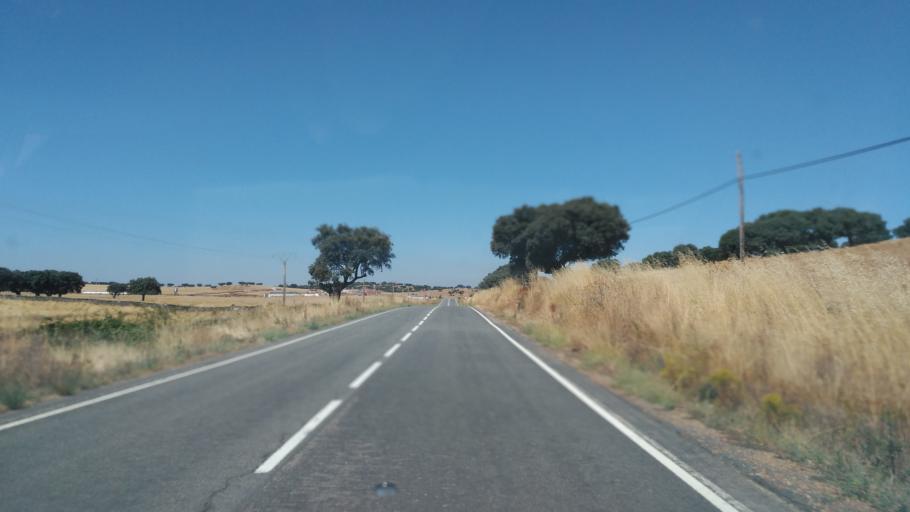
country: ES
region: Castille and Leon
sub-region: Provincia de Salamanca
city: Vecinos
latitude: 40.7922
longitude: -5.9106
